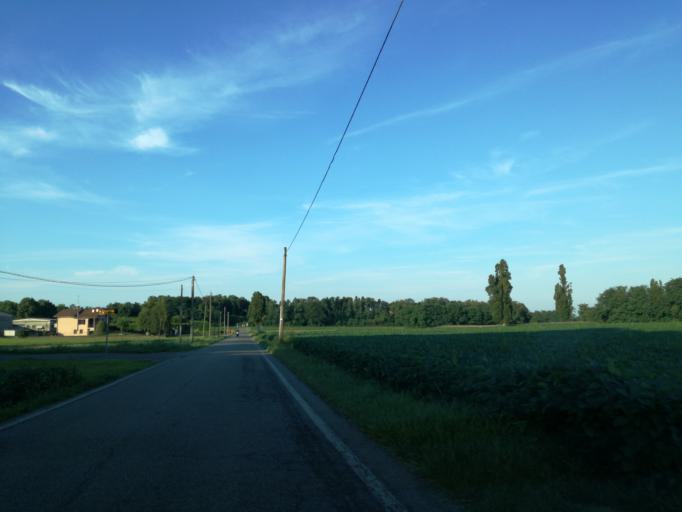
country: IT
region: Lombardy
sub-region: Provincia di Lecco
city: Verderio Inferiore
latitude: 45.6576
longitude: 9.4313
